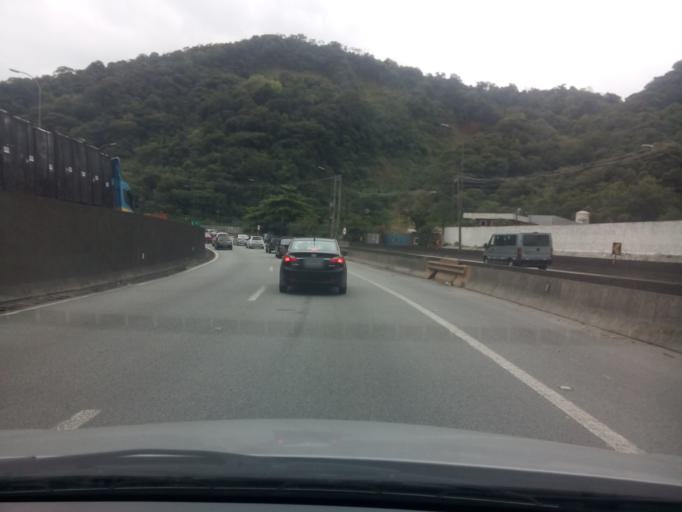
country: BR
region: Sao Paulo
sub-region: Cubatao
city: Cubatao
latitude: -23.8903
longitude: -46.4415
